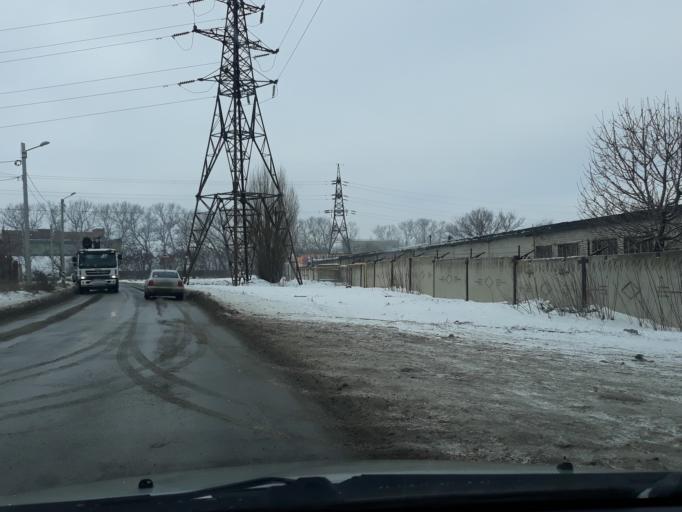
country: RU
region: Rostov
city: Taganrog
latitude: 47.2481
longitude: 38.8877
